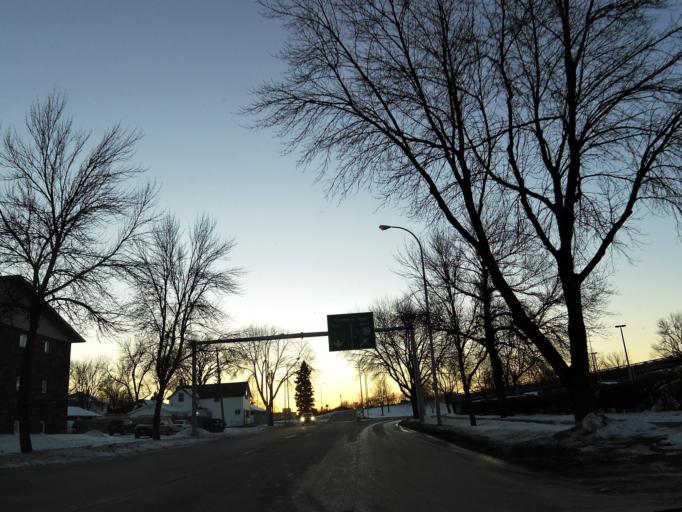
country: US
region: North Dakota
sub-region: Grand Forks County
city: Grand Forks
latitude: 47.9185
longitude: -97.0371
